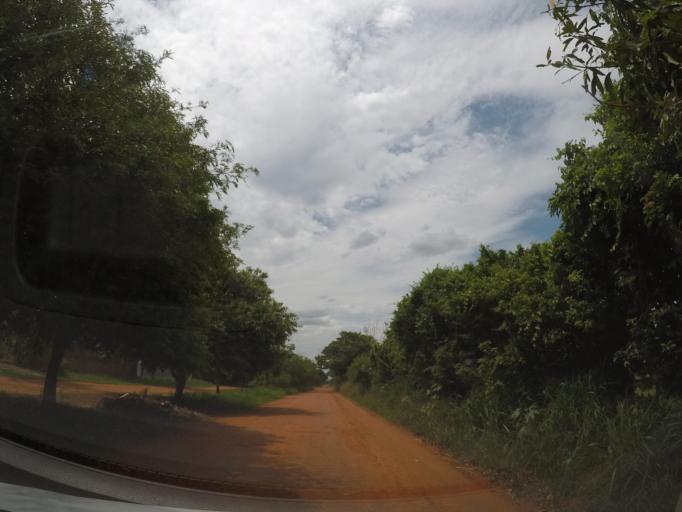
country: BR
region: Sao Paulo
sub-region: Sumare
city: Sumare
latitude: -22.8490
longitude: -47.2930
